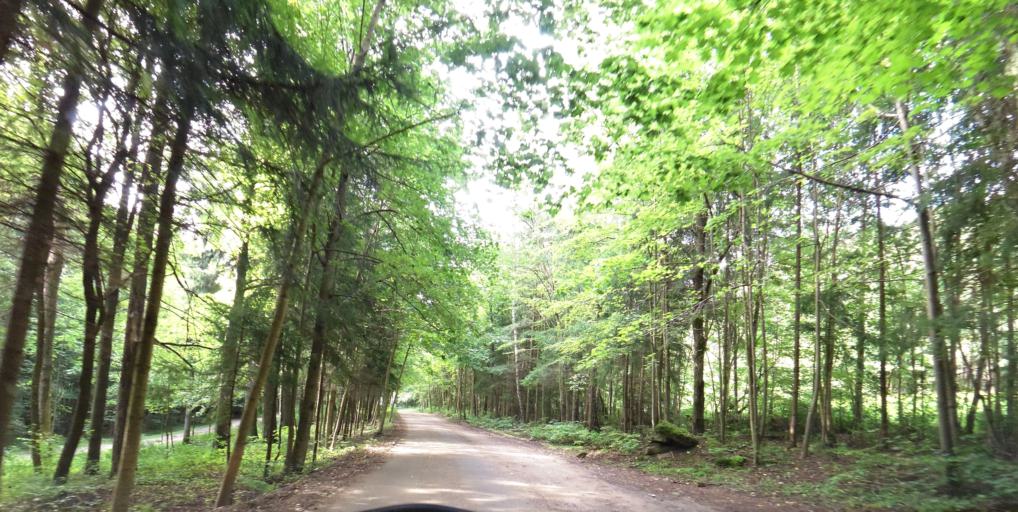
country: LT
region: Vilnius County
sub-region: Vilnius
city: Fabijoniskes
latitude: 54.7380
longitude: 25.2833
